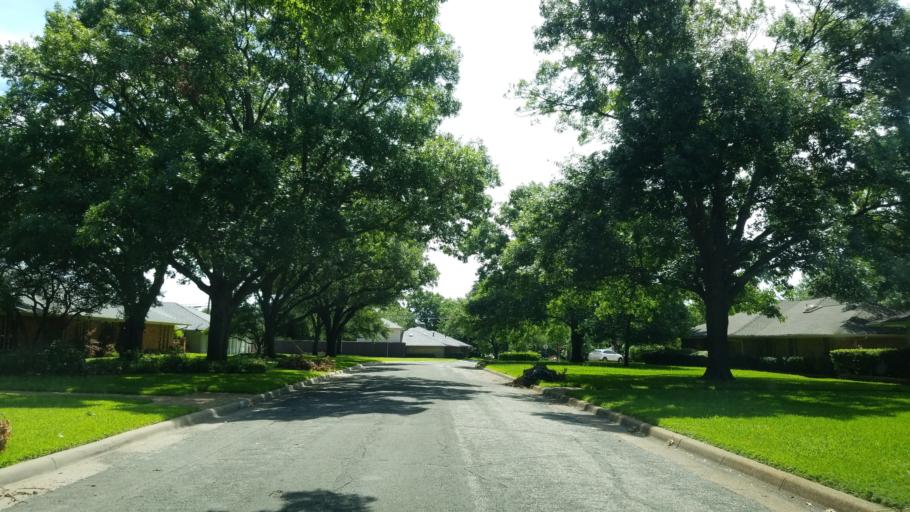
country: US
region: Texas
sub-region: Dallas County
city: Farmers Branch
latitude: 32.9064
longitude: -96.8526
